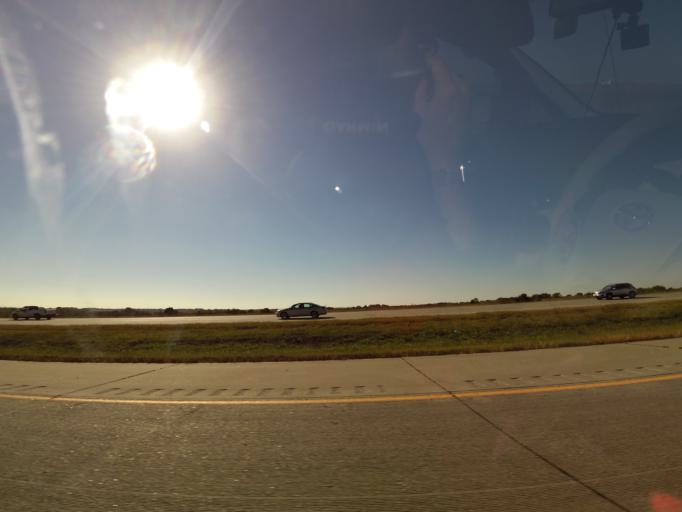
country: US
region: Nebraska
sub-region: Lancaster County
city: Waverly
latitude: 40.9098
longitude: -96.4905
